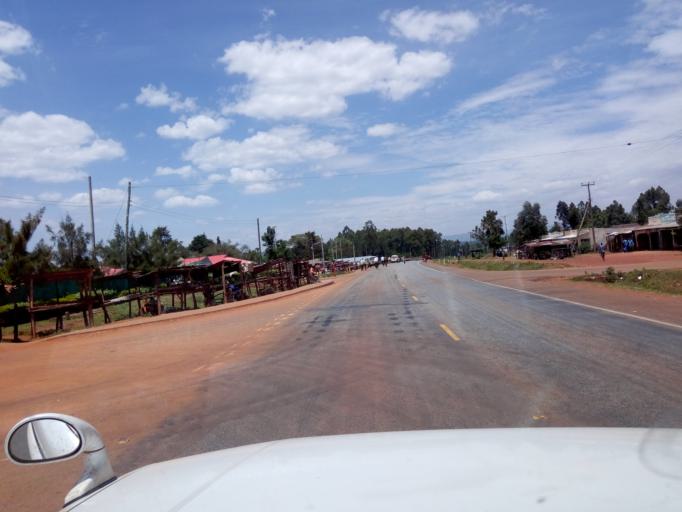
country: KE
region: Bungoma
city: Webuye
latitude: 0.6232
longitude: 34.6918
